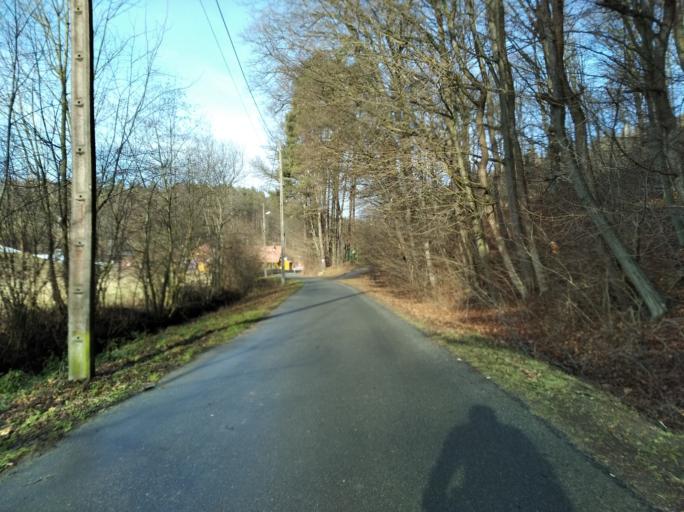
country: PL
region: Subcarpathian Voivodeship
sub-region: Powiat strzyzowski
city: Strzyzow
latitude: 49.8776
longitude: 21.7777
